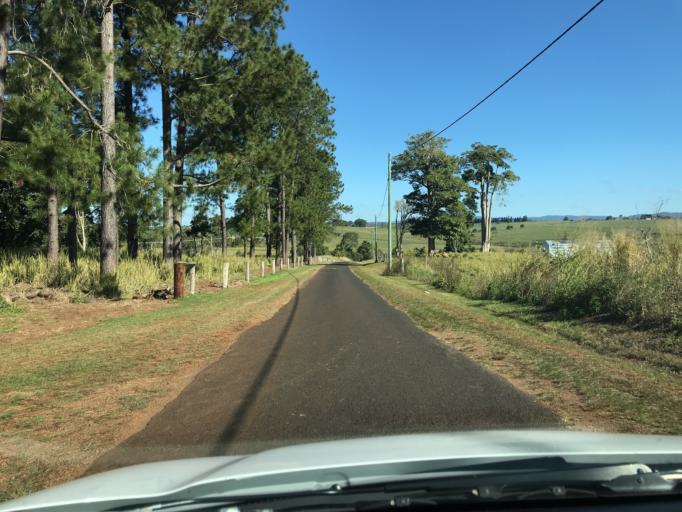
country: AU
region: Queensland
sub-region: Tablelands
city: Atherton
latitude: -17.2930
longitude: 145.5446
